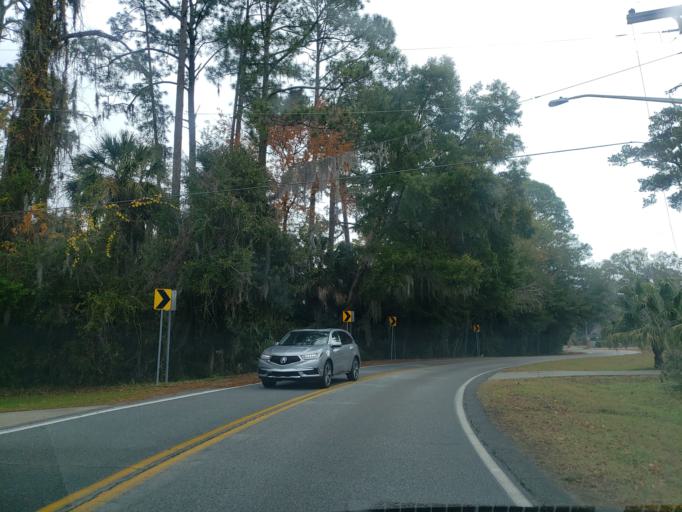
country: US
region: Georgia
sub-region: Chatham County
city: Wilmington Island
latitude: 31.9829
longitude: -80.9966
